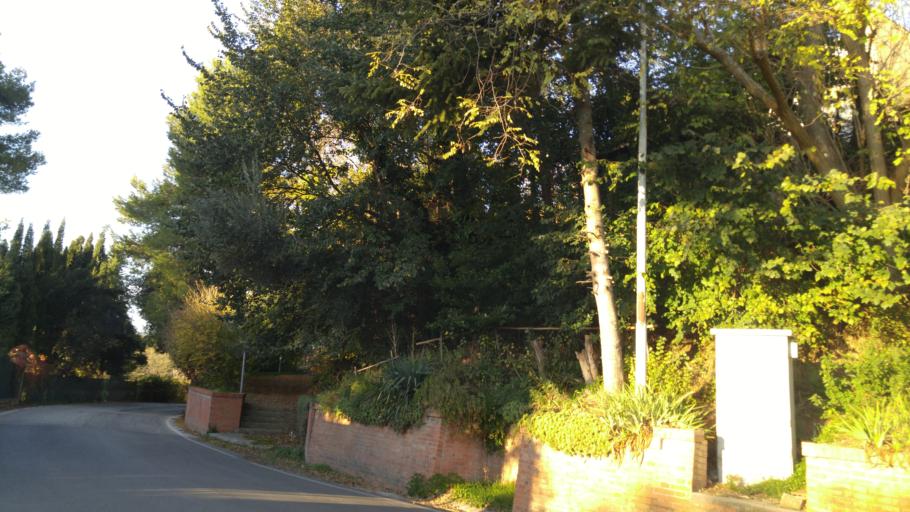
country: IT
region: The Marches
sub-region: Provincia di Pesaro e Urbino
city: Pesaro
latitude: 43.8574
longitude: 12.8860
